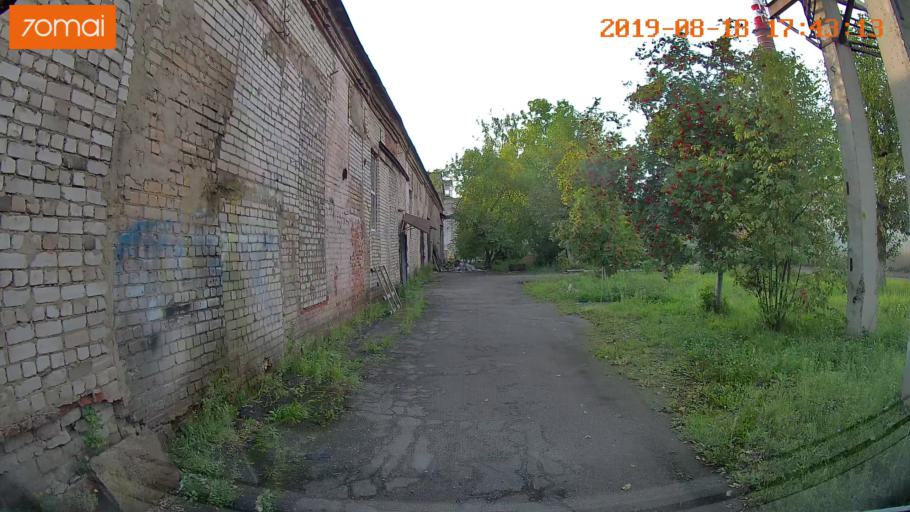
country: RU
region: Ivanovo
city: Kokhma
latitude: 56.9663
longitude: 41.0567
